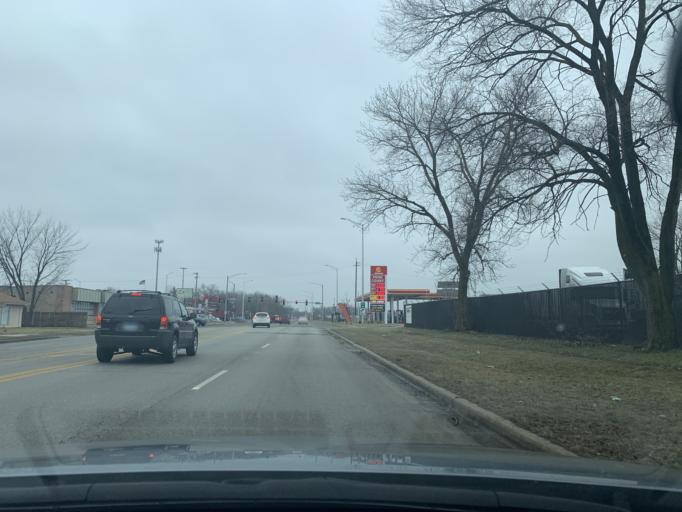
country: US
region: Illinois
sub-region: Cook County
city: University Park
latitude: 41.6023
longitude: -87.6687
